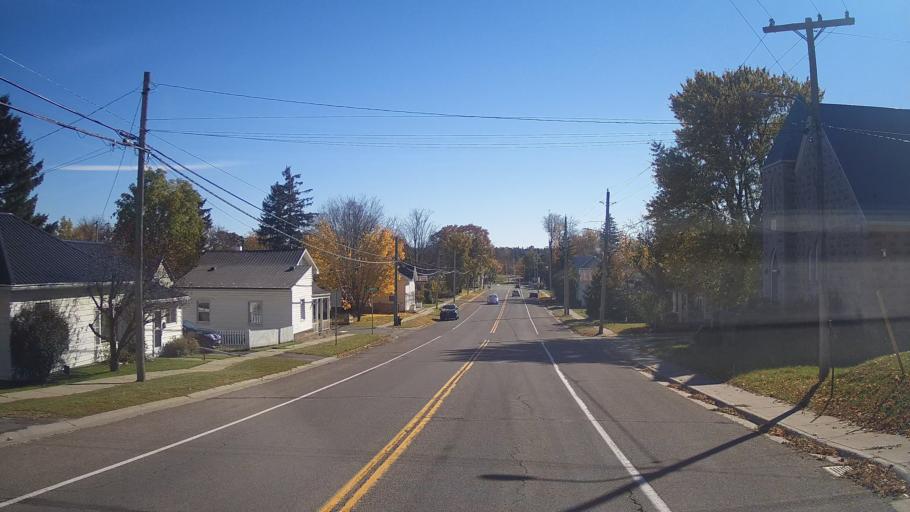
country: CA
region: Ontario
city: Kingston
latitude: 44.4073
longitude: -76.6658
